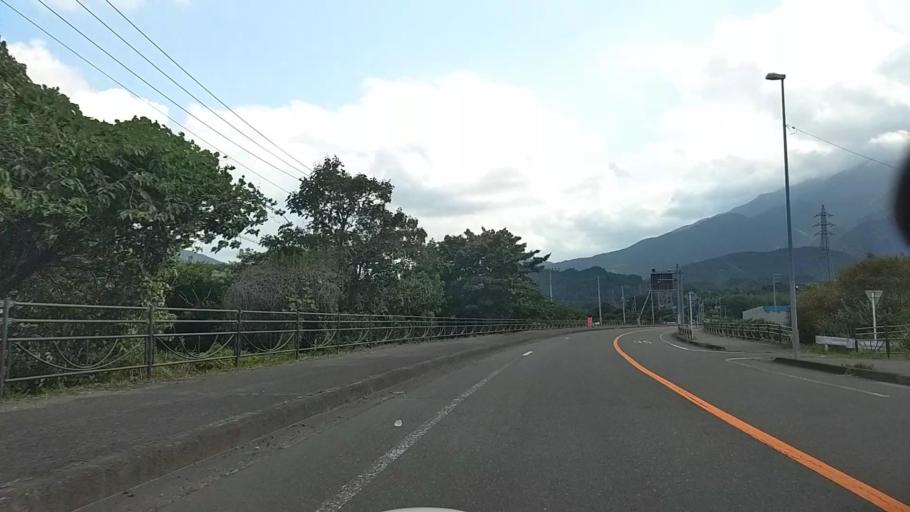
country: JP
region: Shizuoka
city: Fujinomiya
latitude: 35.3078
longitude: 138.4477
